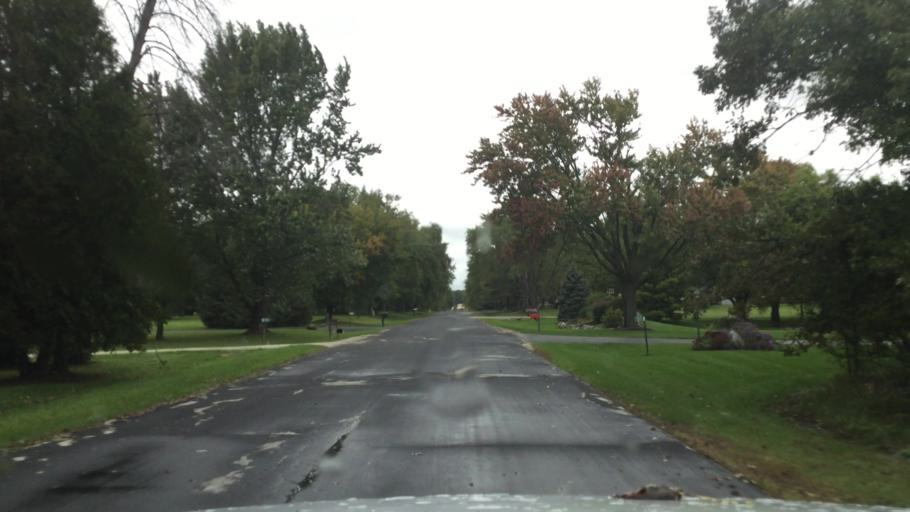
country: US
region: Wisconsin
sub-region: Racine County
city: Waterford
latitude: 42.7580
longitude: -88.1850
